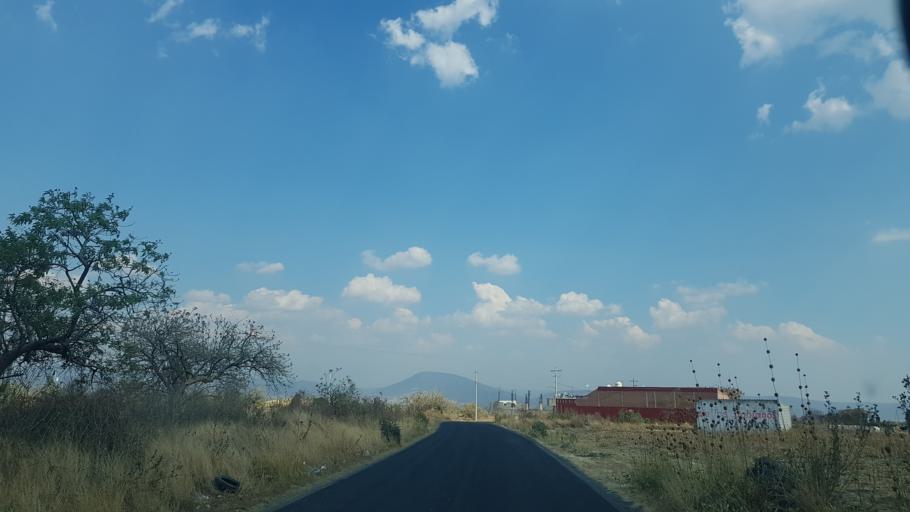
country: MX
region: Puebla
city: Atlixco
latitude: 18.9181
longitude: -98.4812
